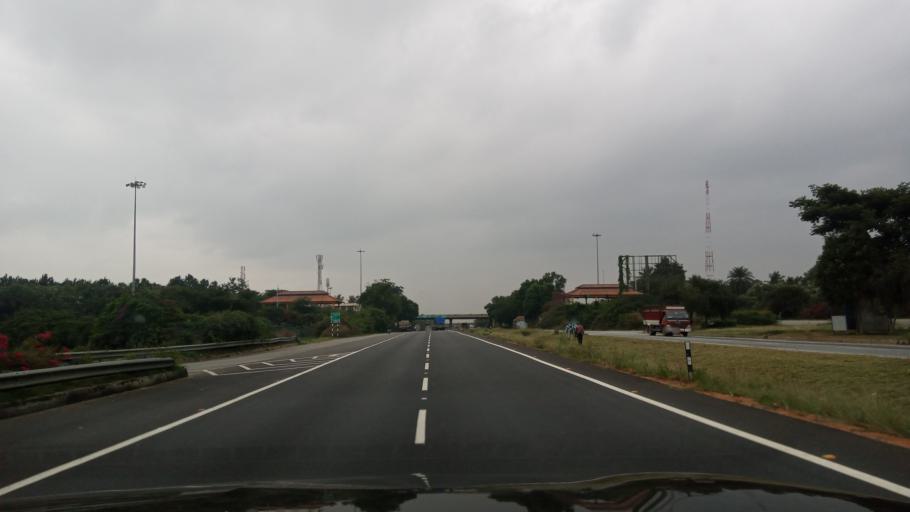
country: IN
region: Karnataka
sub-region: Bangalore Urban
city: Bangalore
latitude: 12.9919
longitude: 77.4729
